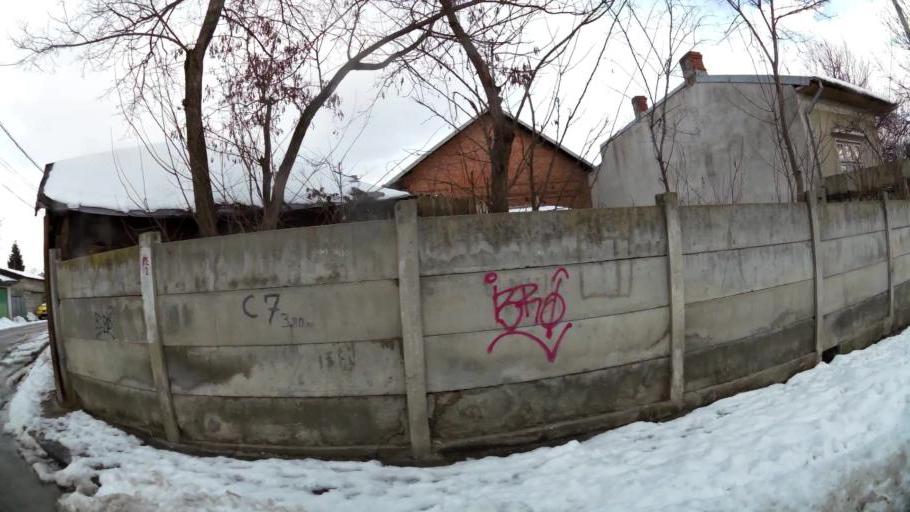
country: RO
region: Ilfov
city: Dobroesti
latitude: 44.4483
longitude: 26.1800
